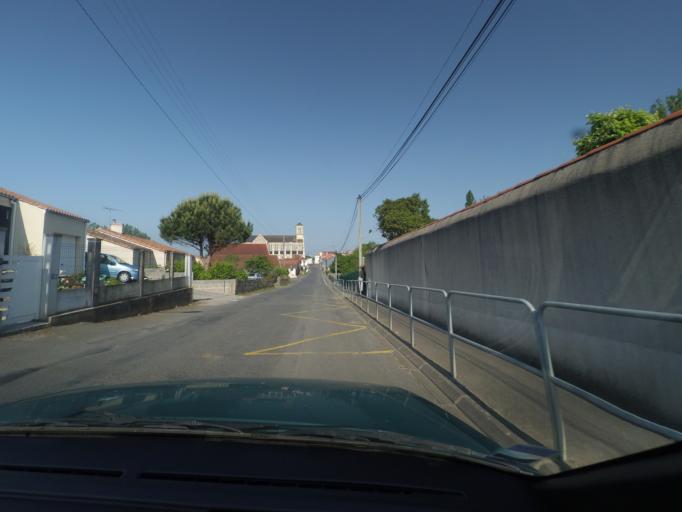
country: FR
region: Pays de la Loire
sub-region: Departement de la Loire-Atlantique
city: Mouzillon
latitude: 47.1401
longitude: -1.2780
